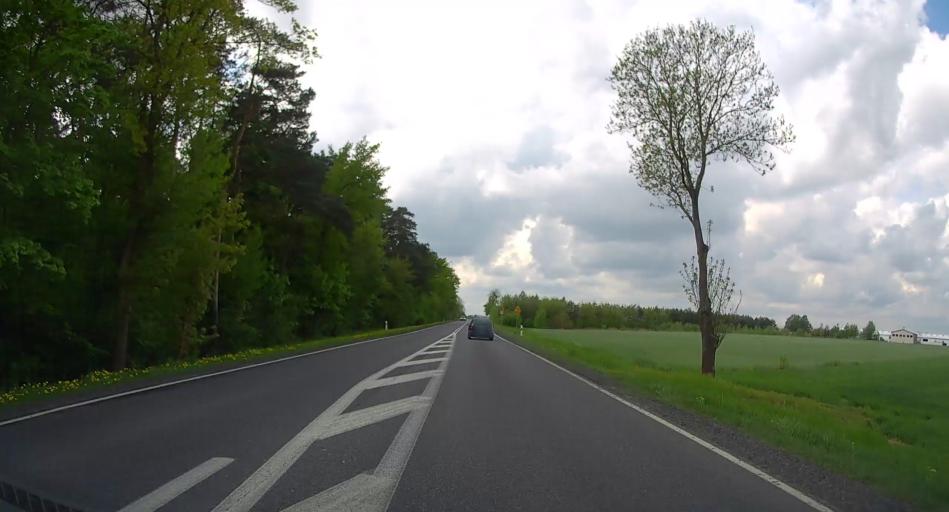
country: PL
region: Masovian Voivodeship
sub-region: Powiat nowodworski
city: Zakroczym
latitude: 52.4449
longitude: 20.5779
